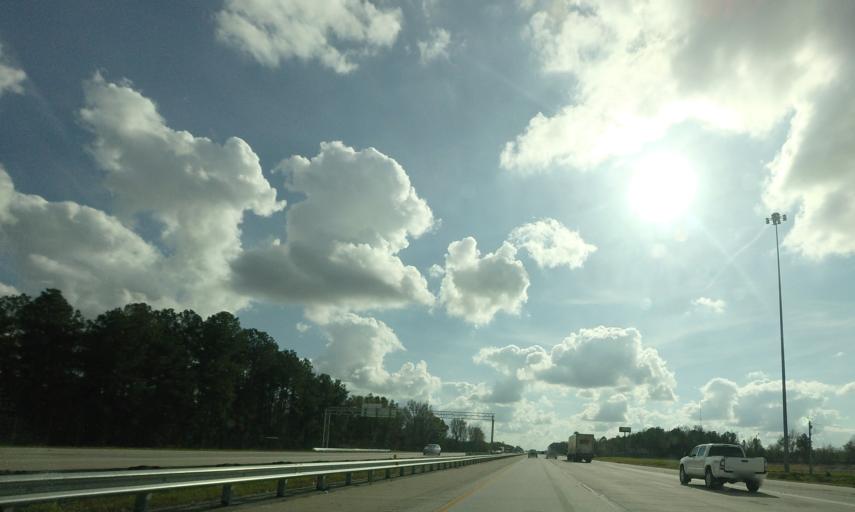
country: US
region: Georgia
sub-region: Dooly County
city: Unadilla
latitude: 32.1894
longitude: -83.7486
